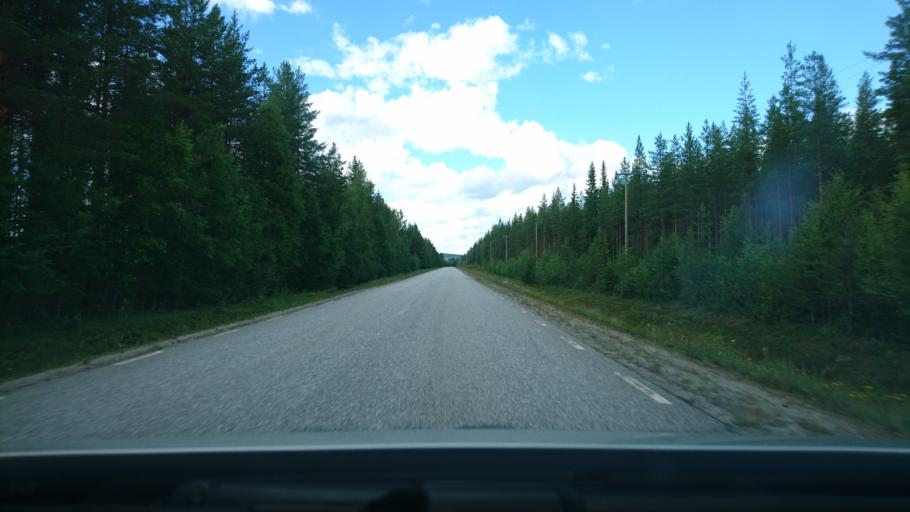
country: SE
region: Vaesterbotten
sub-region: Asele Kommun
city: Asele
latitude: 63.9853
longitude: 17.2651
